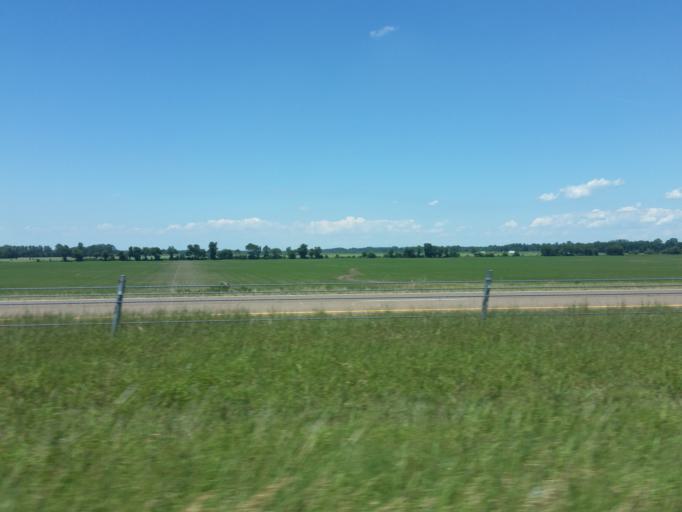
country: US
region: Missouri
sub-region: Pemiscot County
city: Caruthersville
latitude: 36.0949
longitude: -89.5943
